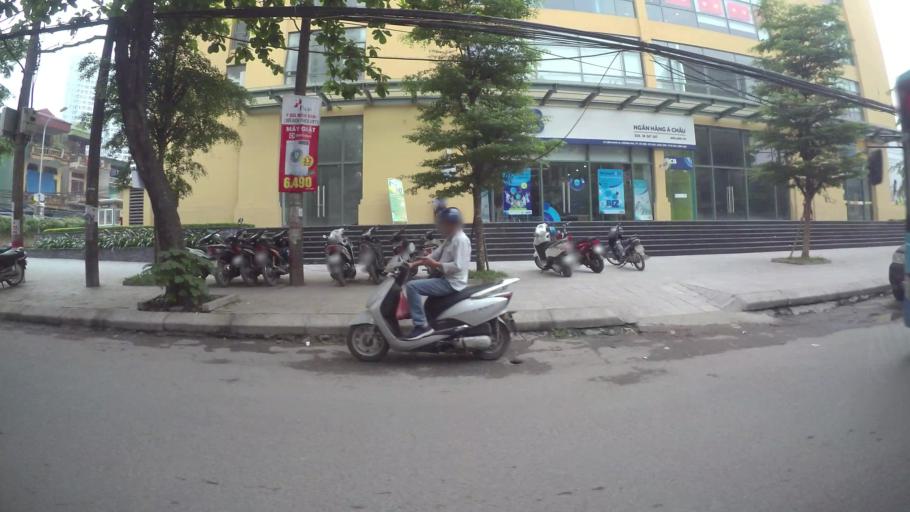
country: VN
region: Ha Noi
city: Hai BaTrung
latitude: 20.9892
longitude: 105.8656
